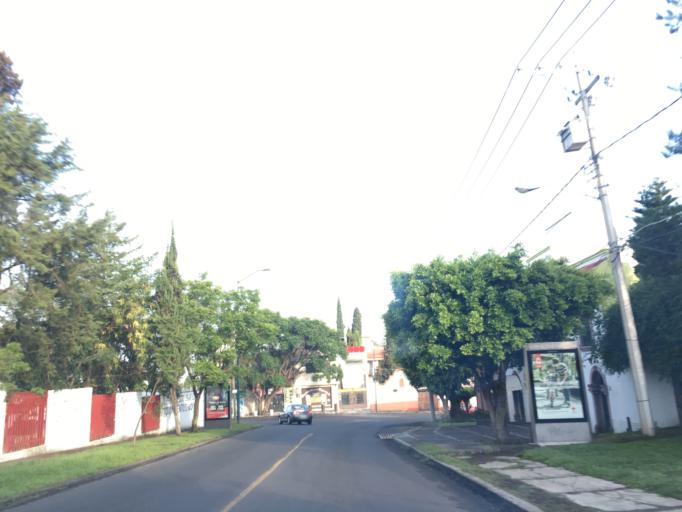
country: MX
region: Michoacan
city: Morelia
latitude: 19.6794
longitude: -101.1968
